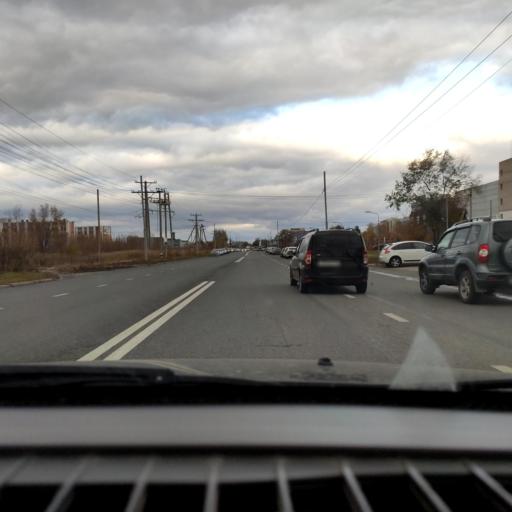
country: RU
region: Samara
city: Tol'yatti
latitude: 53.5552
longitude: 49.2938
